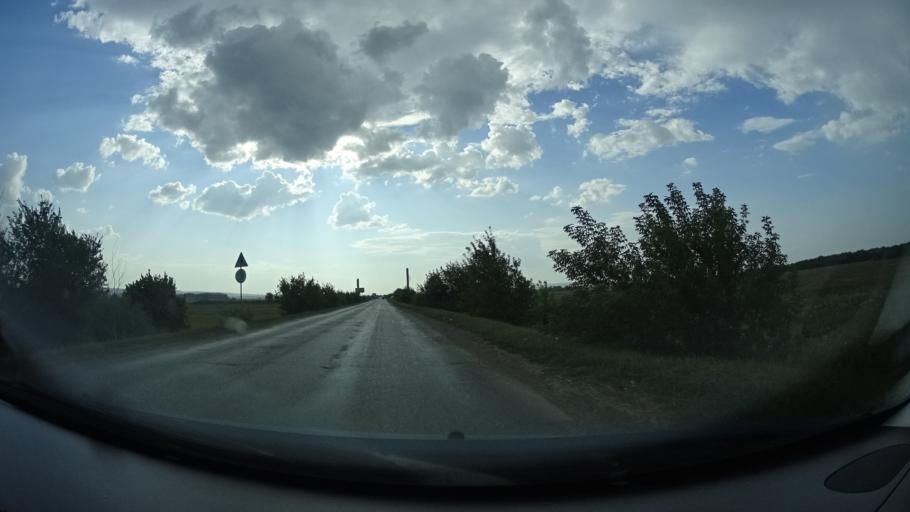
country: RU
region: Bashkortostan
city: Oktyabr'skiy
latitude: 54.4856
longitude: 53.4306
